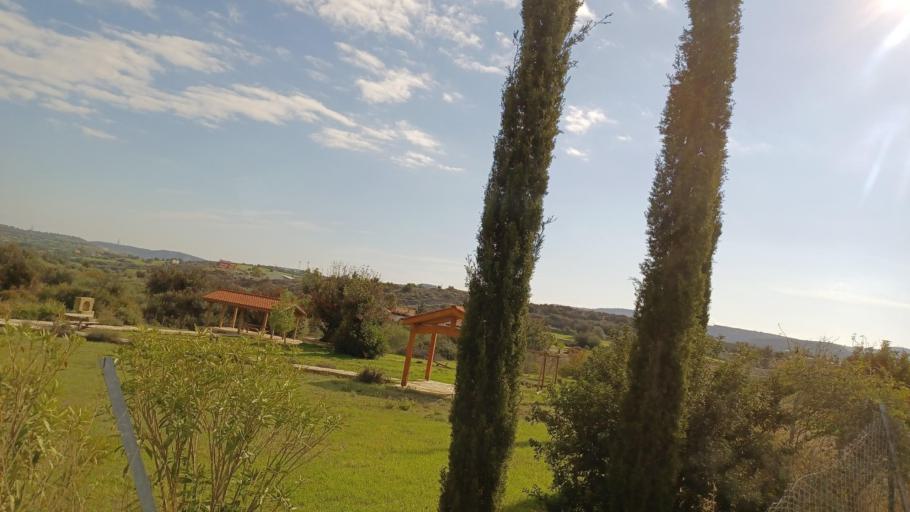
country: CY
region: Larnaka
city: Kofinou
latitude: 34.8155
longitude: 33.3467
